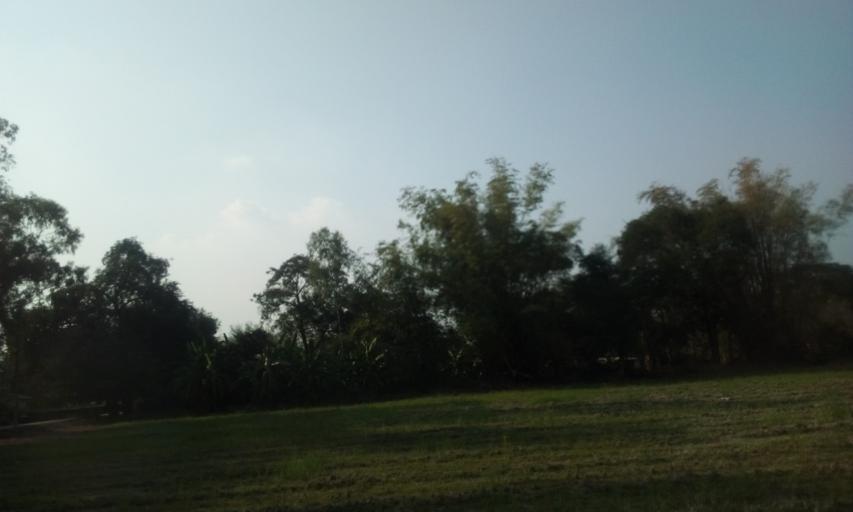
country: TH
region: Sing Buri
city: Sing Buri
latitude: 14.8357
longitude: 100.4014
